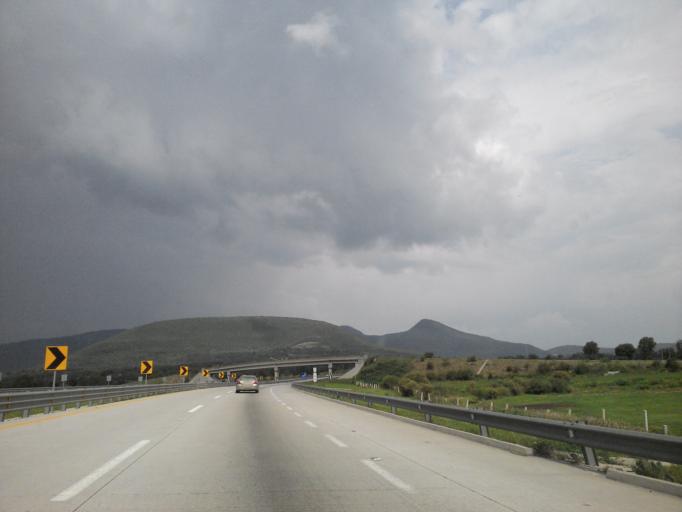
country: MX
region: Hidalgo
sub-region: Atitalaquia
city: Tezoquipa
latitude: 20.0608
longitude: -99.1983
